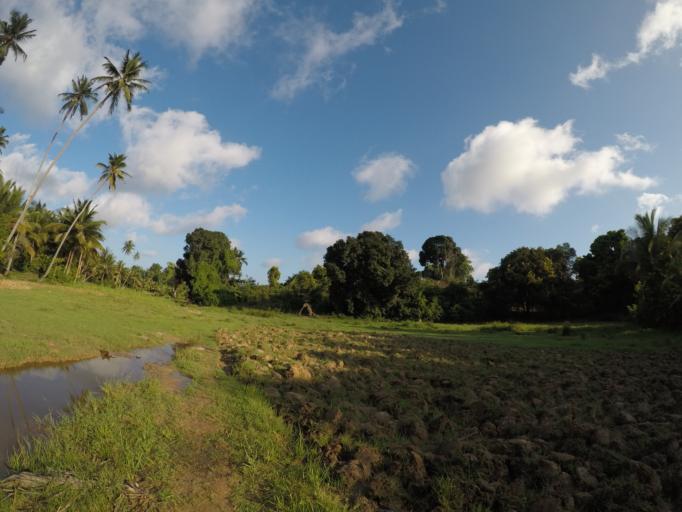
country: TZ
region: Pemba South
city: Mtambile
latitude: -5.3882
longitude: 39.7430
